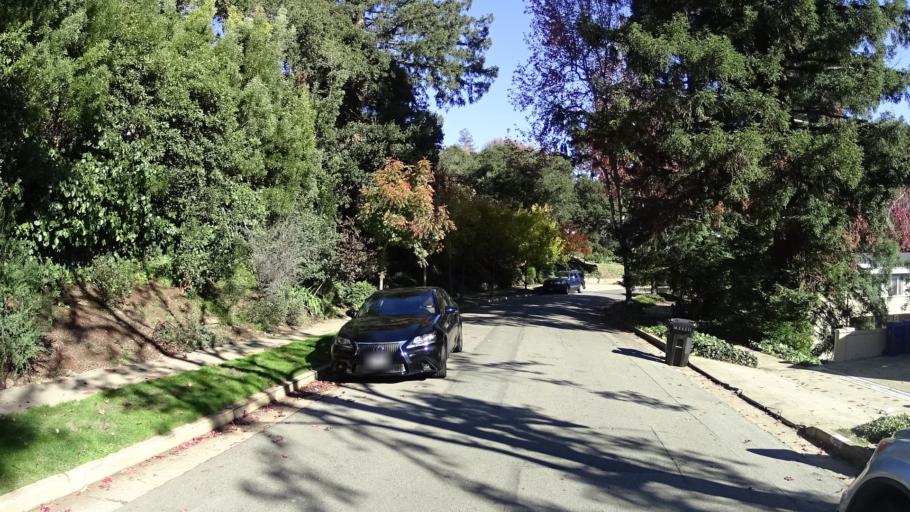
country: US
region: California
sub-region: Alameda County
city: Piedmont
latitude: 37.8164
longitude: -122.2157
